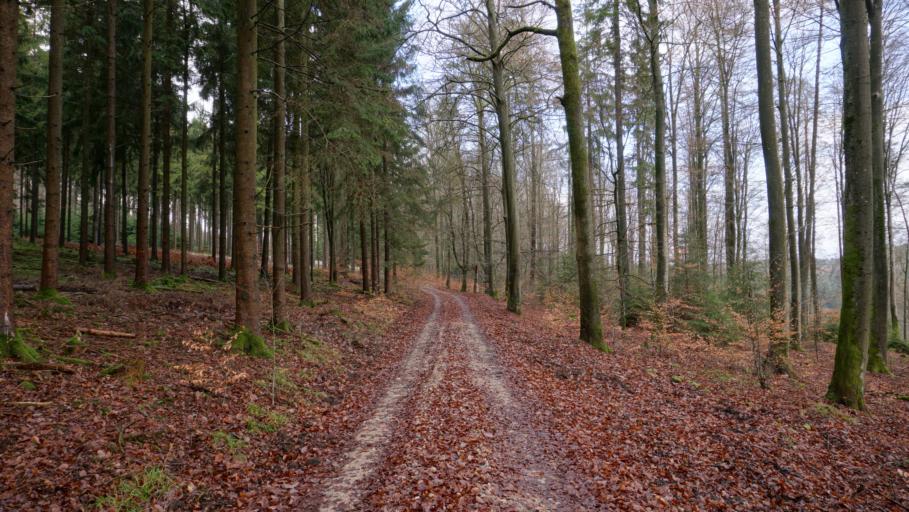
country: DE
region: Baden-Wuerttemberg
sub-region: Karlsruhe Region
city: Fahrenbach
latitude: 49.4315
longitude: 9.1176
